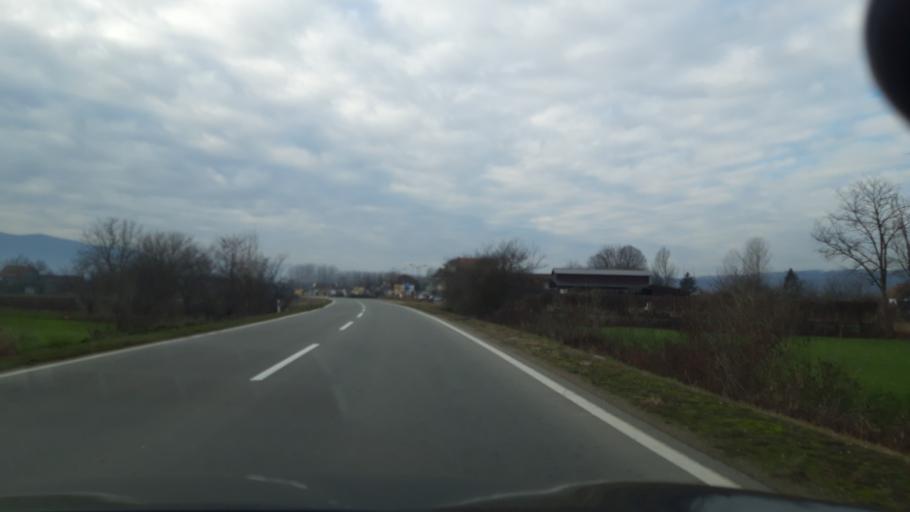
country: RS
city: Lipnicki Sor
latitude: 44.5666
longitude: 19.2038
